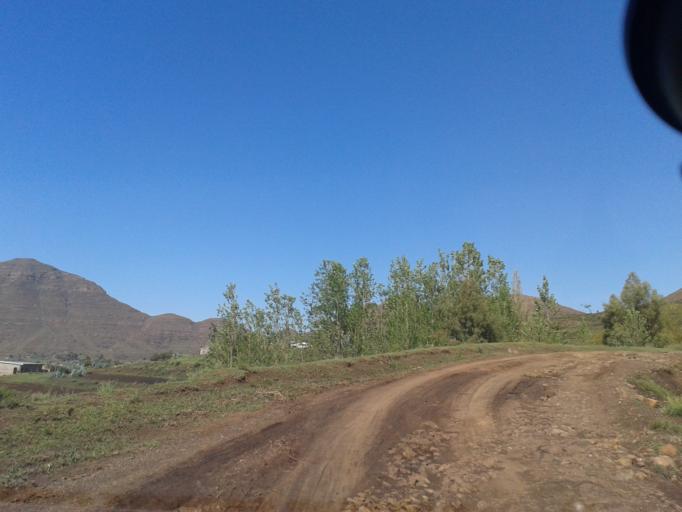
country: LS
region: Maseru
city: Nako
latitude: -29.8447
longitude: 27.5615
